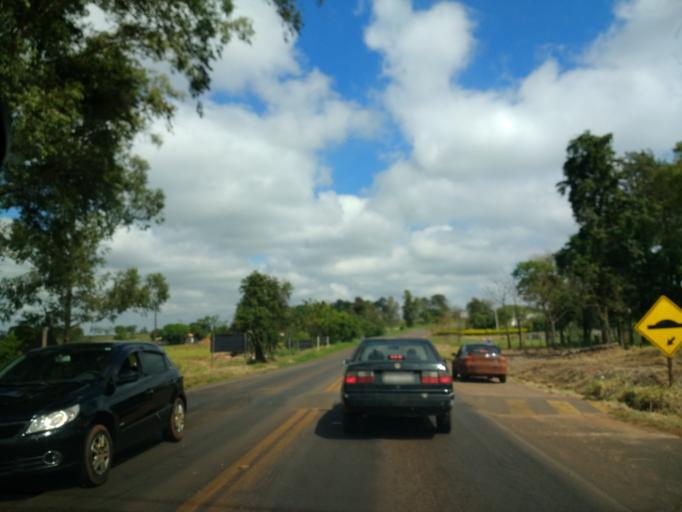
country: BR
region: Parana
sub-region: Cruzeiro Do Oeste
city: Cruzeiro do Oeste
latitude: -23.7962
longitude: -53.0489
